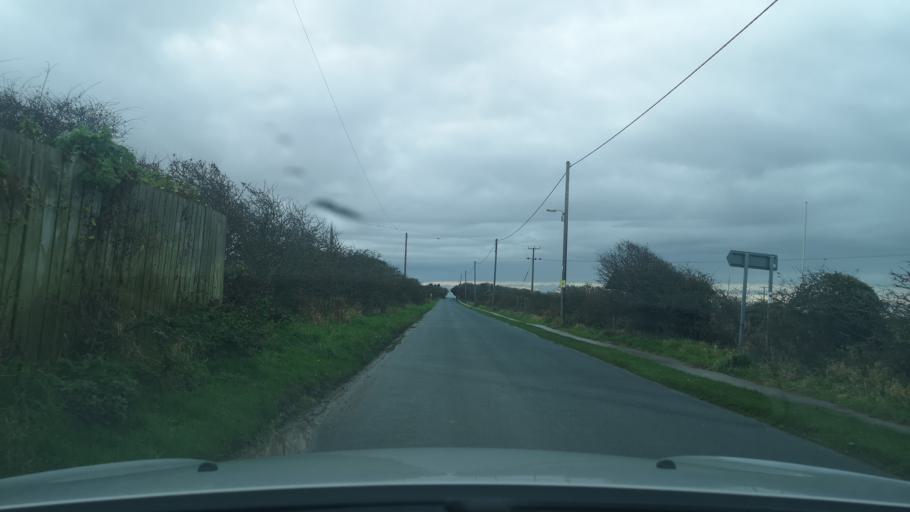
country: GB
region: England
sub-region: East Riding of Yorkshire
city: Easington
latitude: 53.6201
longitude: 0.1388
